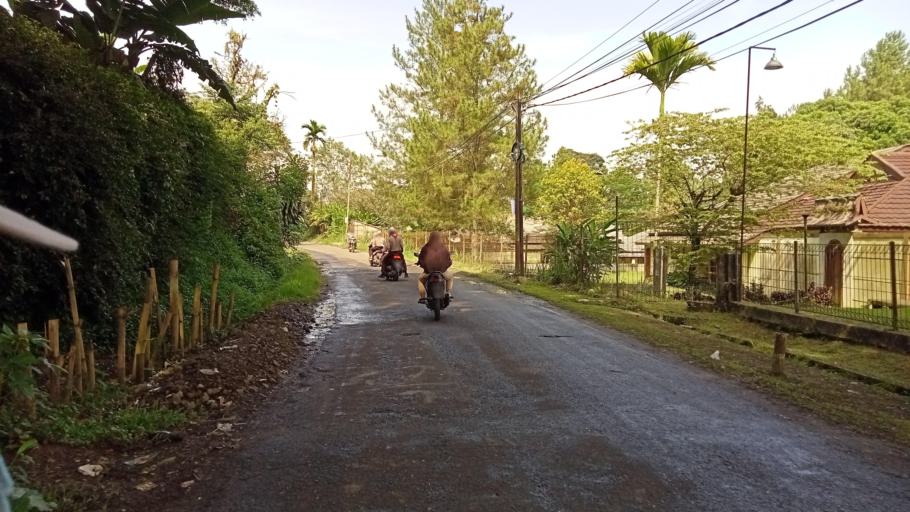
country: ID
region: West Java
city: Caringin
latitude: -6.6472
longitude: 106.9091
